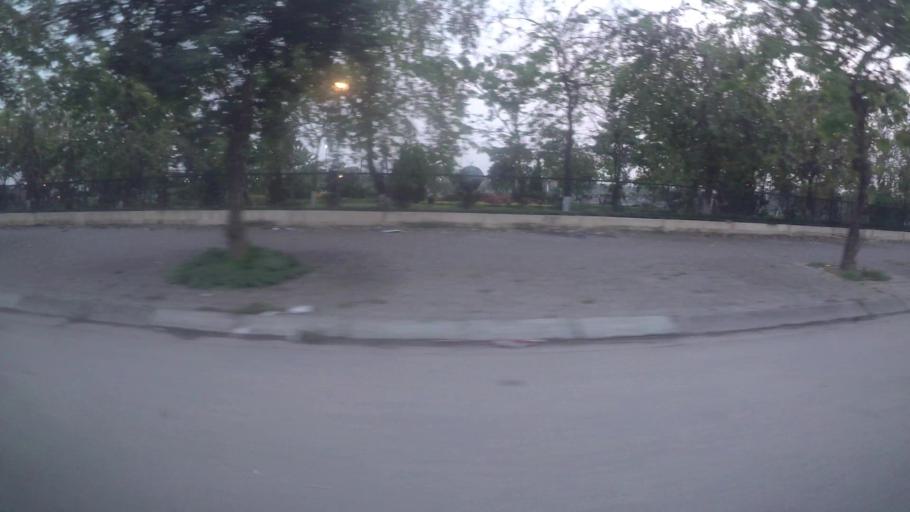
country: VN
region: Ha Noi
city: Tay Ho
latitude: 21.0653
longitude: 105.7897
